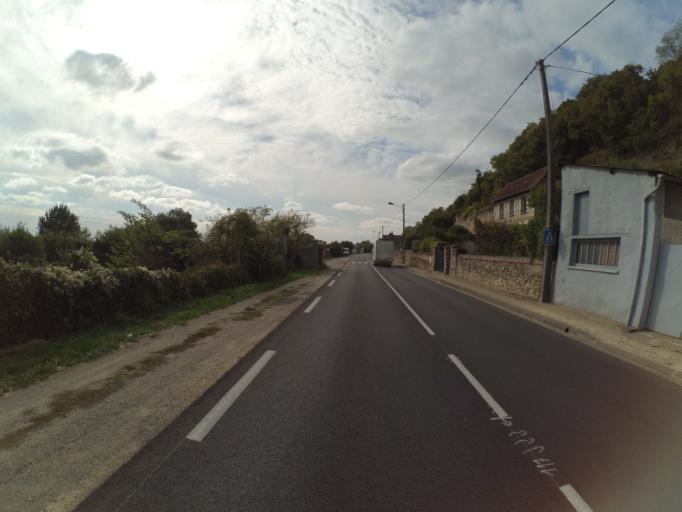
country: FR
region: Centre
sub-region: Departement d'Indre-et-Loire
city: Langeais
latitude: 47.3192
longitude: 0.3947
